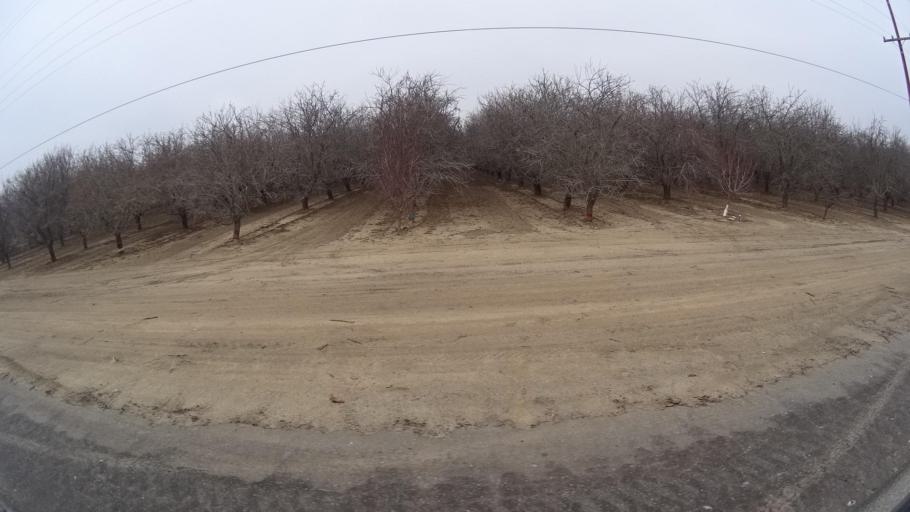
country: US
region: California
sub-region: Kern County
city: Maricopa
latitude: 35.0938
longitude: -119.2823
